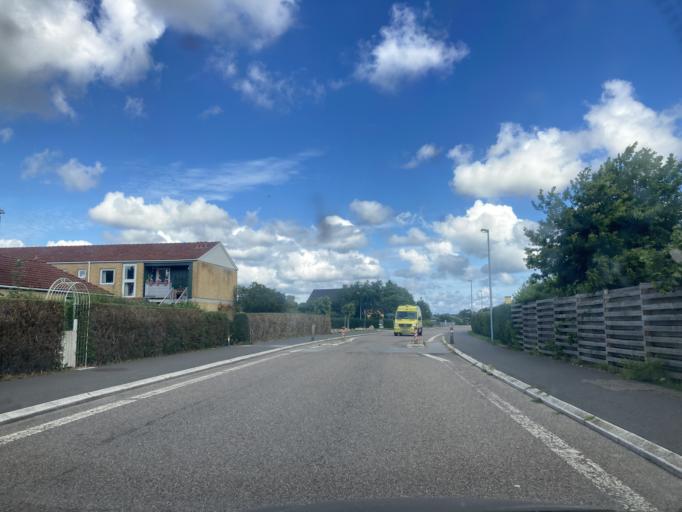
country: DK
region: Capital Region
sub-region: Halsnaes Kommune
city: Frederiksvaerk
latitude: 55.9825
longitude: 12.0134
